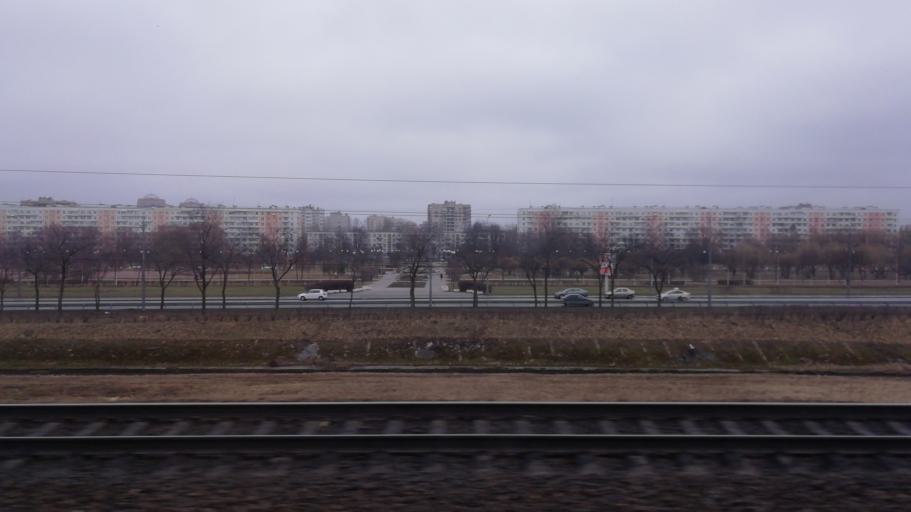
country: RU
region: St.-Petersburg
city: Kupchino
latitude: 59.8627
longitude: 30.3600
